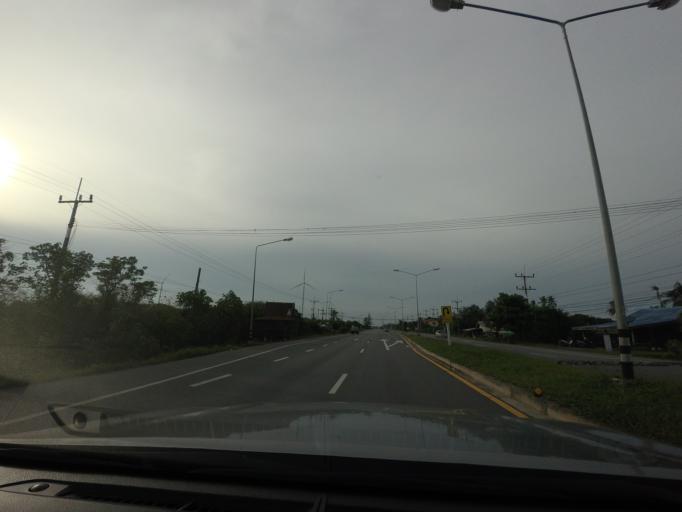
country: TH
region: Nakhon Si Thammarat
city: Hua Sai
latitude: 7.9783
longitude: 100.3264
